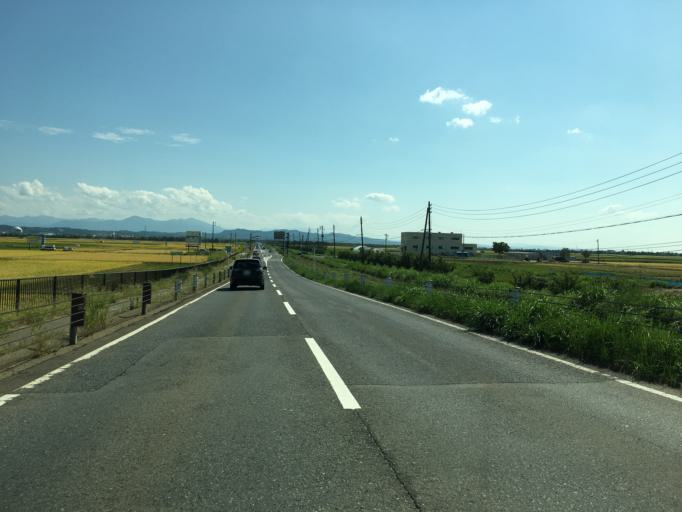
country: JP
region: Niigata
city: Kameda-honcho
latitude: 37.8339
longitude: 139.0966
